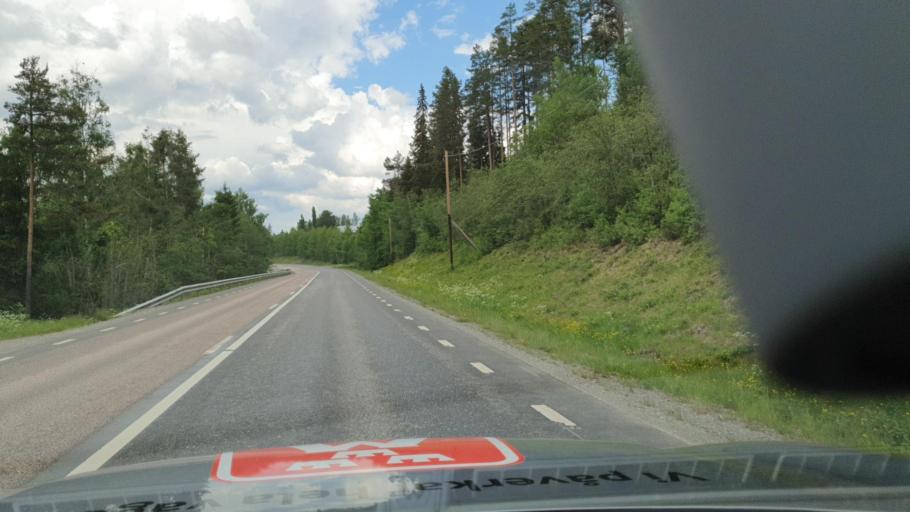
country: SE
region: Vaesternorrland
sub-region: Solleftea Kommun
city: Solleftea
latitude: 63.2021
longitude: 17.2339
